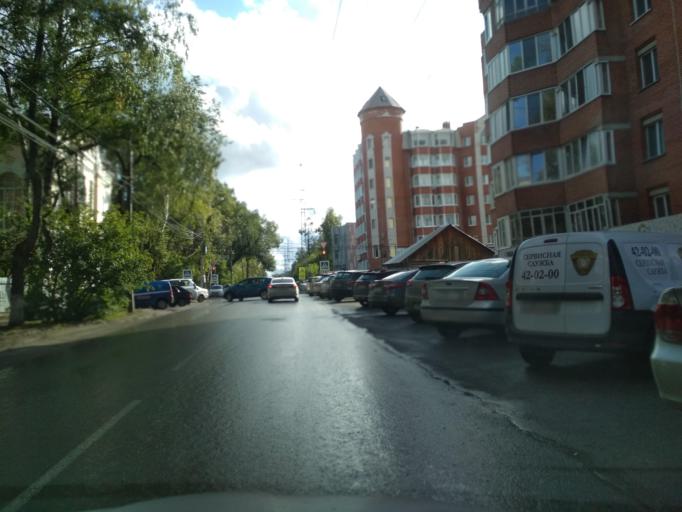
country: RU
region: Tomsk
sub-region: Tomskiy Rayon
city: Tomsk
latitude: 56.4744
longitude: 84.9758
